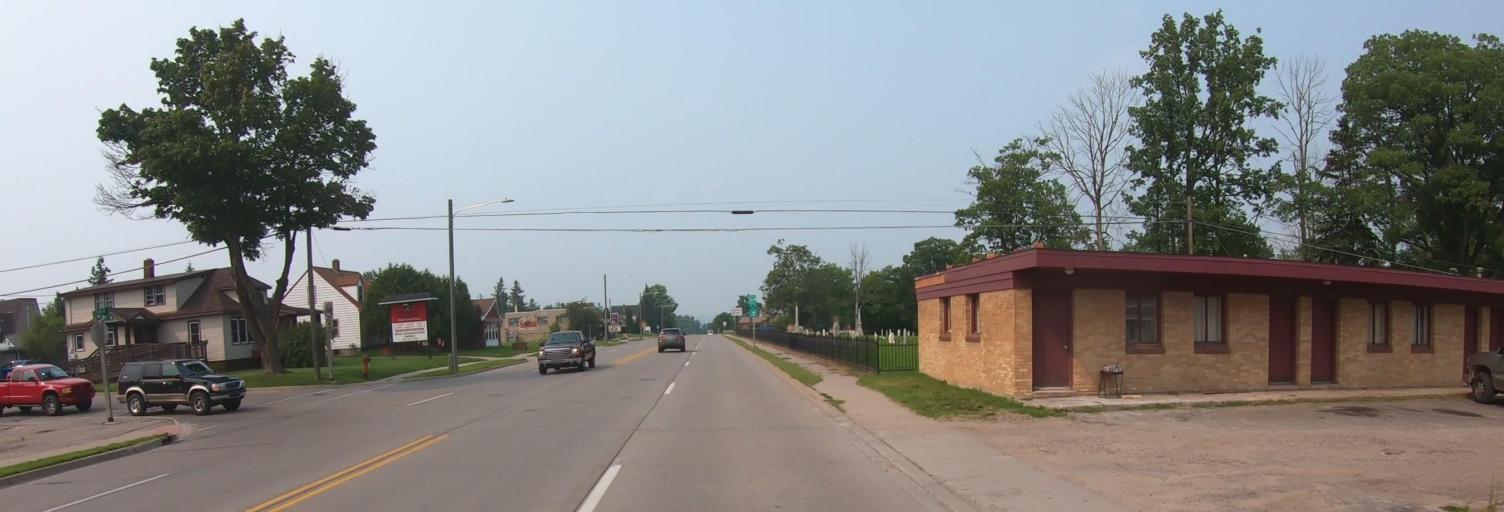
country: US
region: Michigan
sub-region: Chippewa County
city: Sault Ste. Marie
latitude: 46.4843
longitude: -84.3537
